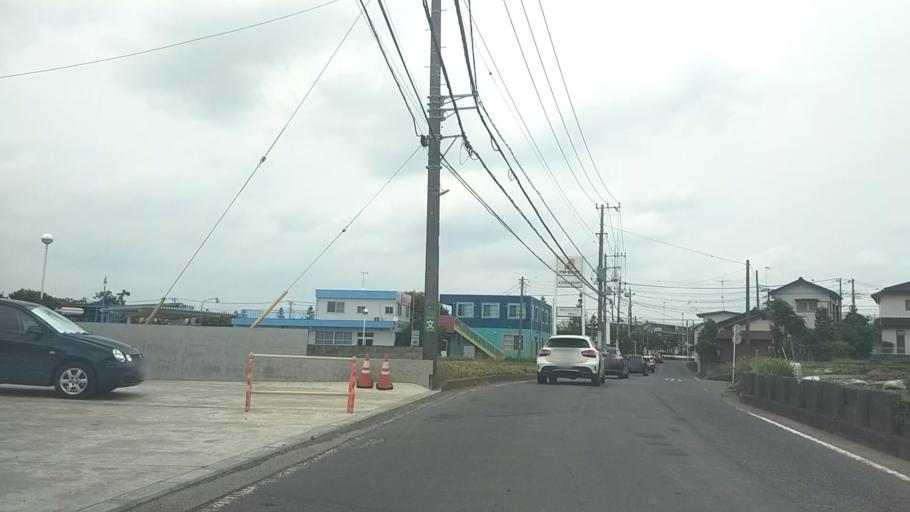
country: JP
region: Kanagawa
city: Fujisawa
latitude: 35.3636
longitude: 139.4356
